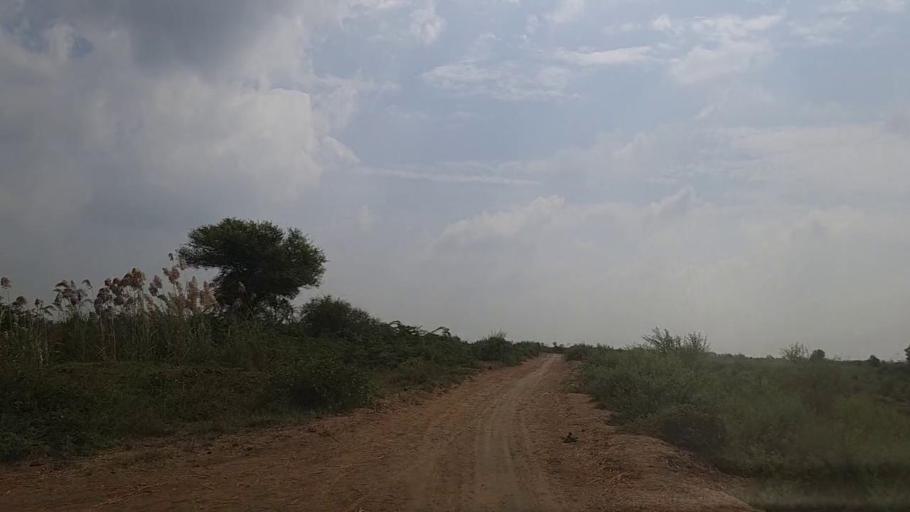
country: PK
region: Sindh
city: Mirpur Batoro
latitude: 24.6087
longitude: 68.1386
